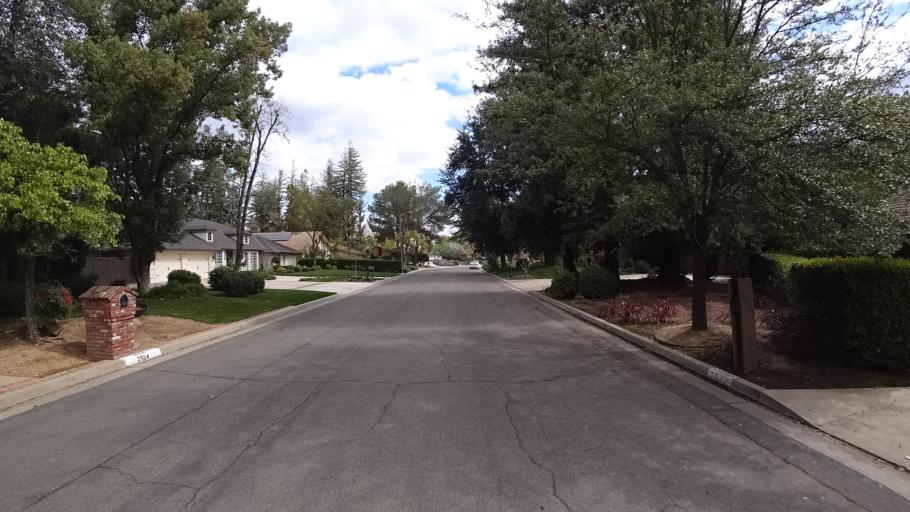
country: US
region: California
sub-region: Fresno County
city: Fresno
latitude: 36.8286
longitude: -119.8383
